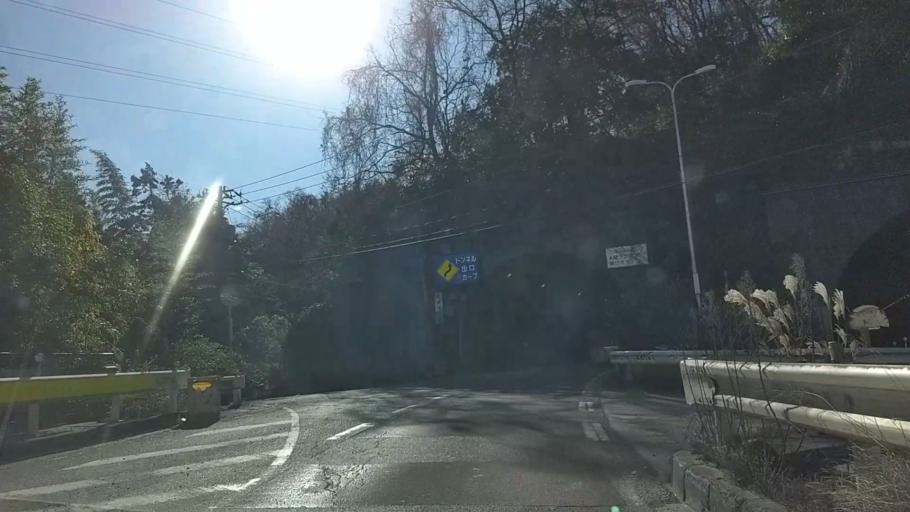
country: JP
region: Shizuoka
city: Gotemba
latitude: 35.3691
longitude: 139.0217
